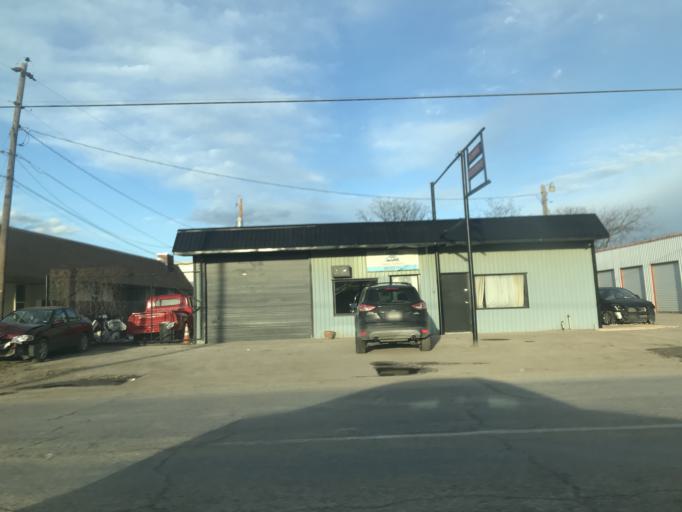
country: US
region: Texas
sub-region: Tom Green County
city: San Angelo
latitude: 31.4967
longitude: -100.4589
